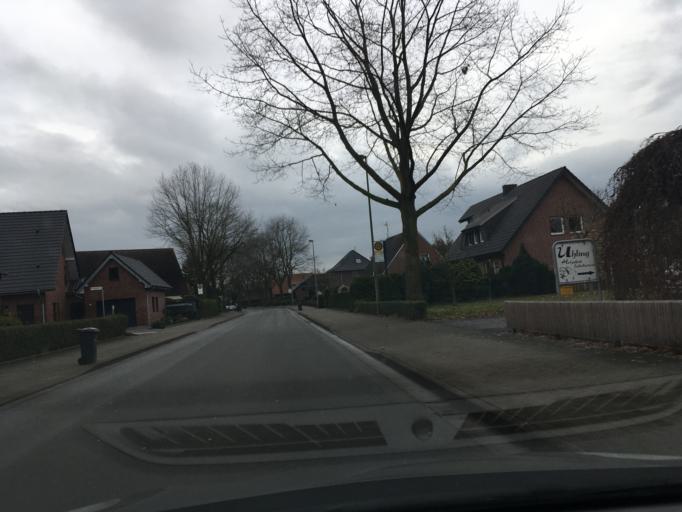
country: DE
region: North Rhine-Westphalia
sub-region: Regierungsbezirk Munster
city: Ahaus
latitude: 52.0964
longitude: 6.9789
